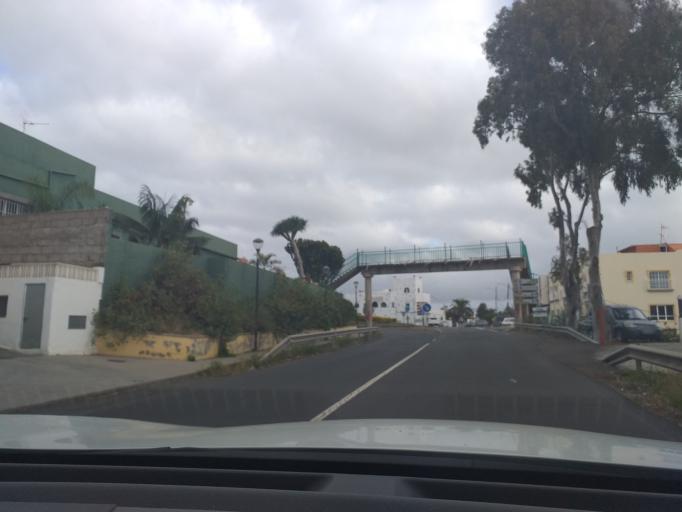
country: ES
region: Canary Islands
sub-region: Provincia de Las Palmas
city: Arucas
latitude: 28.1116
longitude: -15.5101
